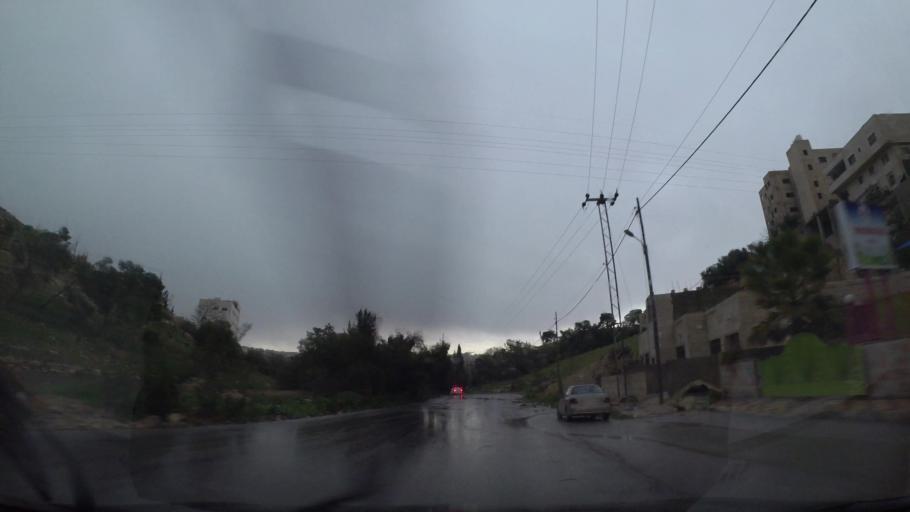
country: JO
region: Amman
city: Amman
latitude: 31.9921
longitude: 35.9740
